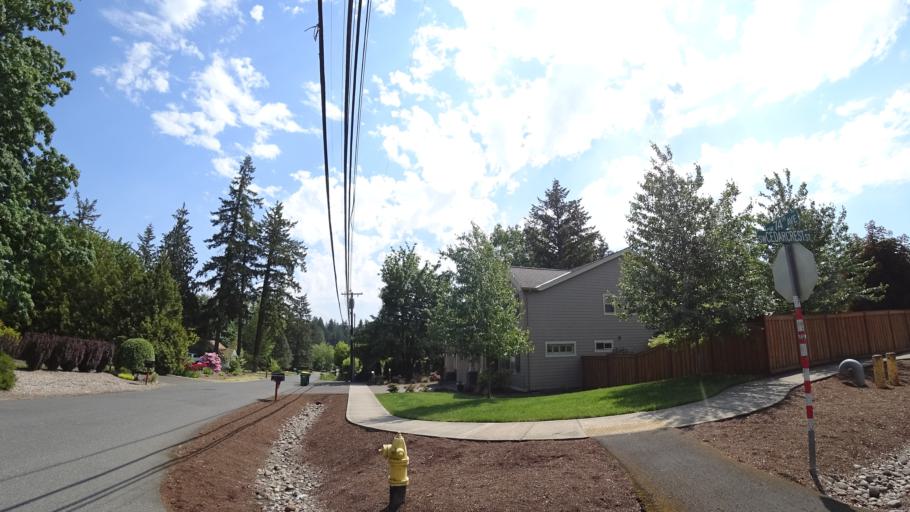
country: US
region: Oregon
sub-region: Washington County
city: Metzger
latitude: 45.4527
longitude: -122.7528
